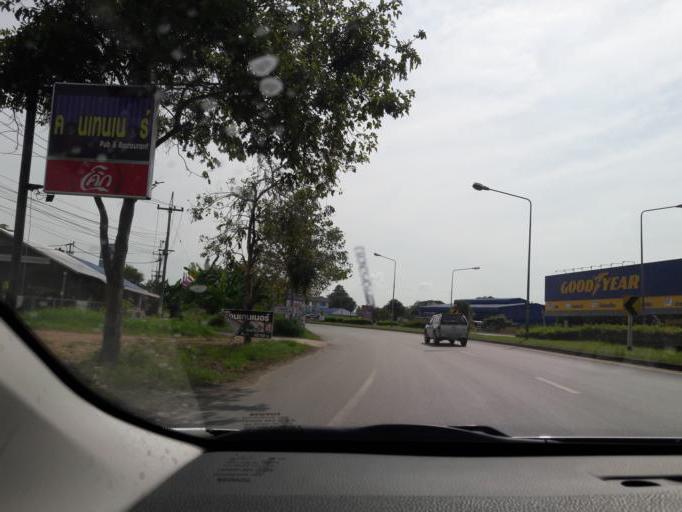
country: TH
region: Ang Thong
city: Ang Thong
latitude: 14.5910
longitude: 100.4406
